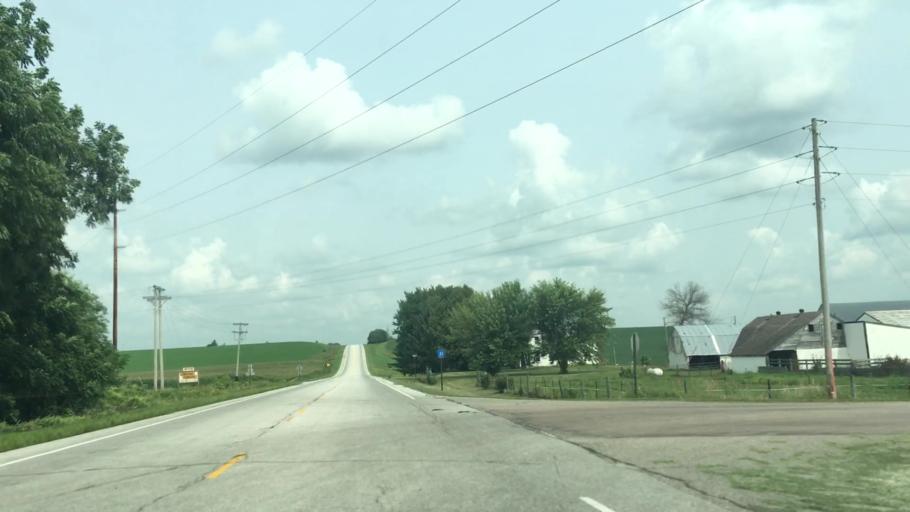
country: US
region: Minnesota
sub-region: Fillmore County
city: Harmony
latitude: 43.5945
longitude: -91.9297
